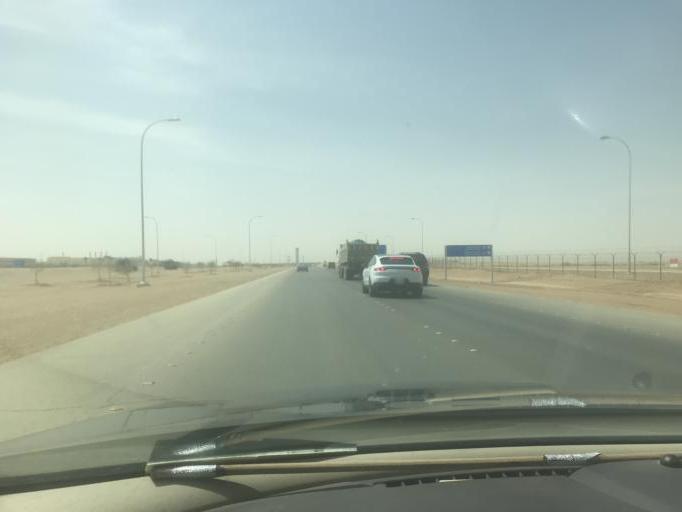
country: SA
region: Ar Riyad
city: Riyadh
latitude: 24.9758
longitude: 46.6869
